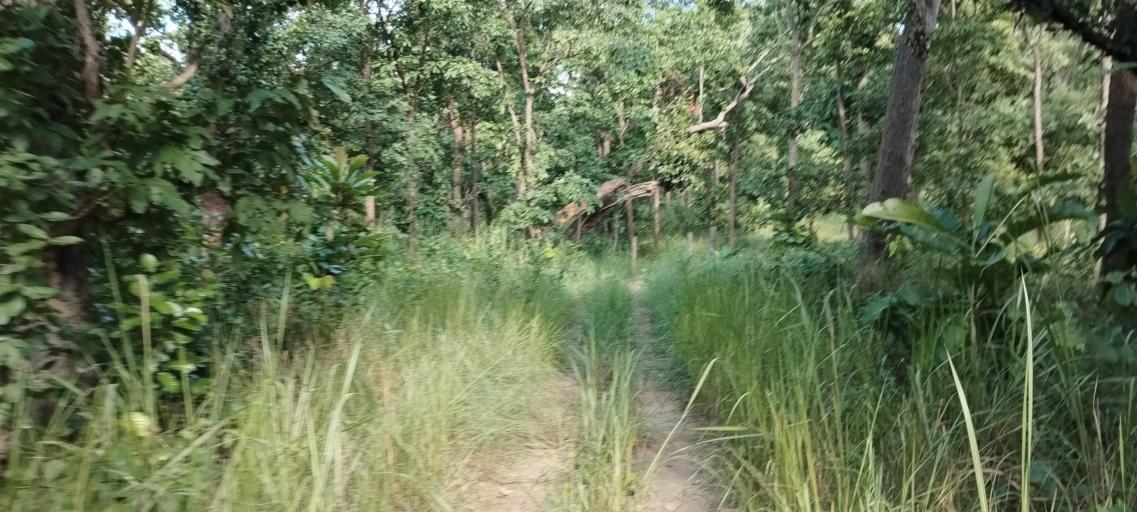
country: NP
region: Far Western
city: Tikapur
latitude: 28.5519
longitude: 81.2823
